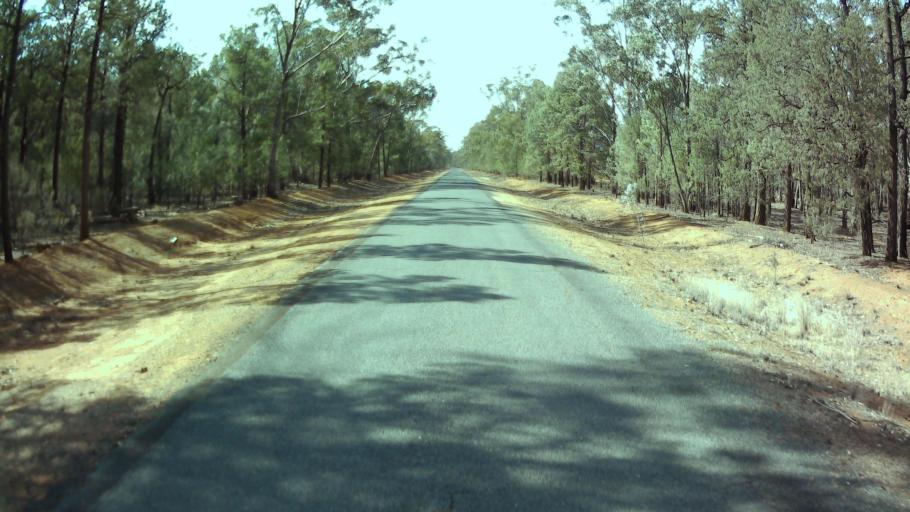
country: AU
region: New South Wales
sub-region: Weddin
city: Grenfell
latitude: -33.7170
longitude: 148.0260
